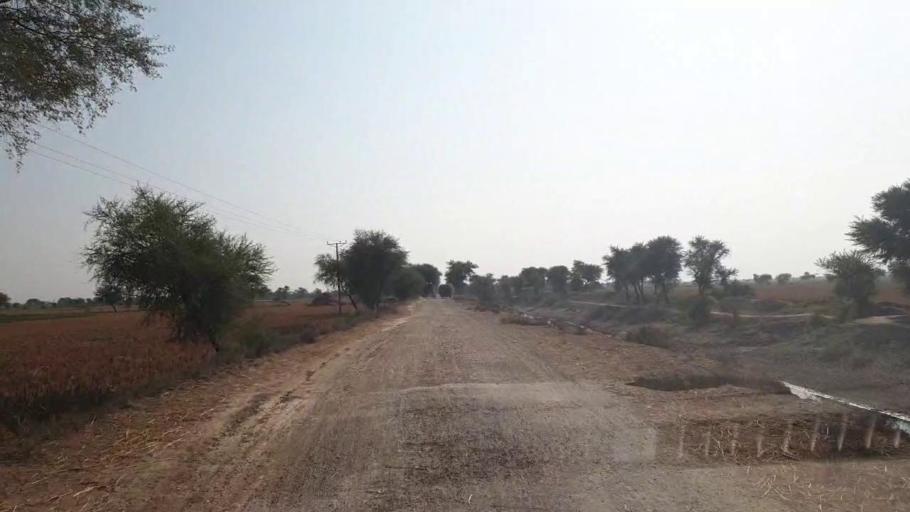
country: PK
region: Sindh
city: Kario
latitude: 24.9084
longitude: 68.6492
